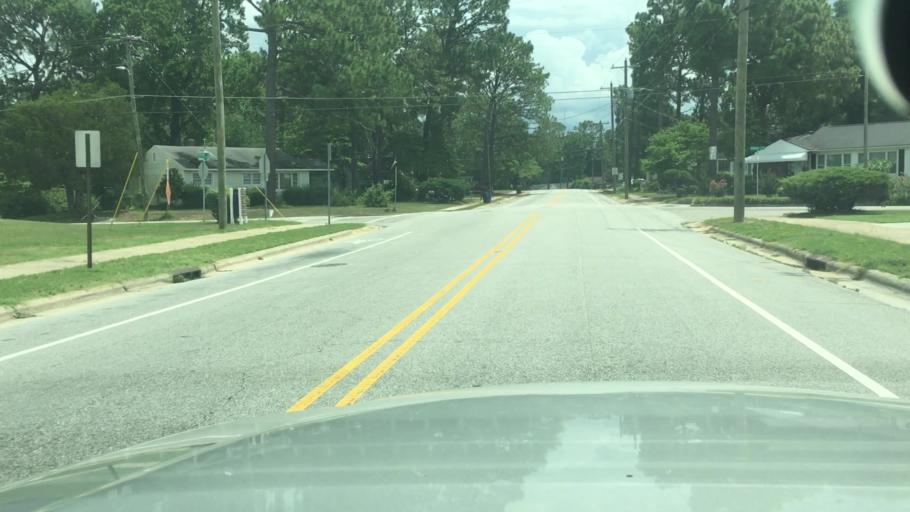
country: US
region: North Carolina
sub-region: Cumberland County
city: Fayetteville
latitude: 35.0831
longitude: -78.8966
